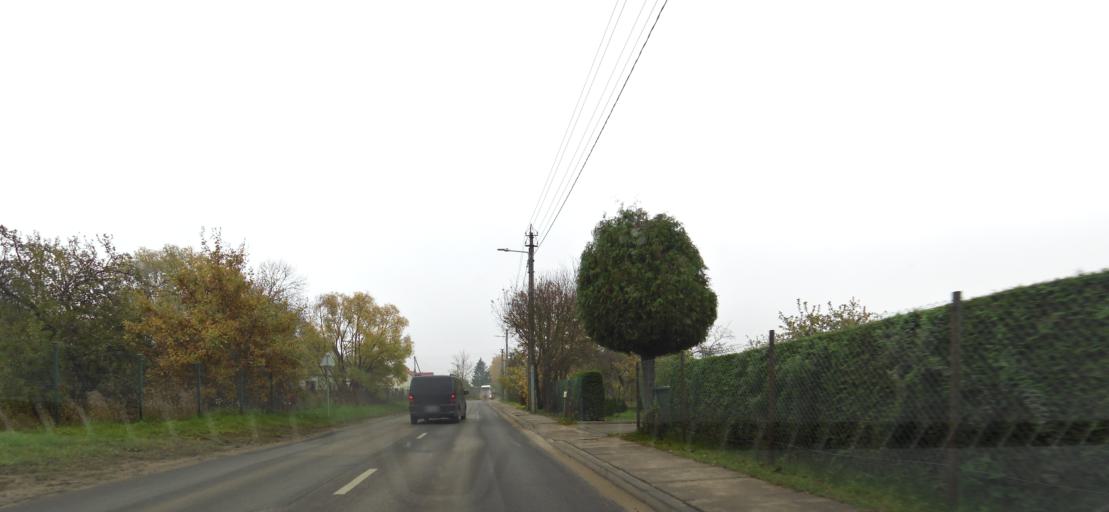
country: LT
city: Skaidiskes
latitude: 54.6598
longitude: 25.3600
